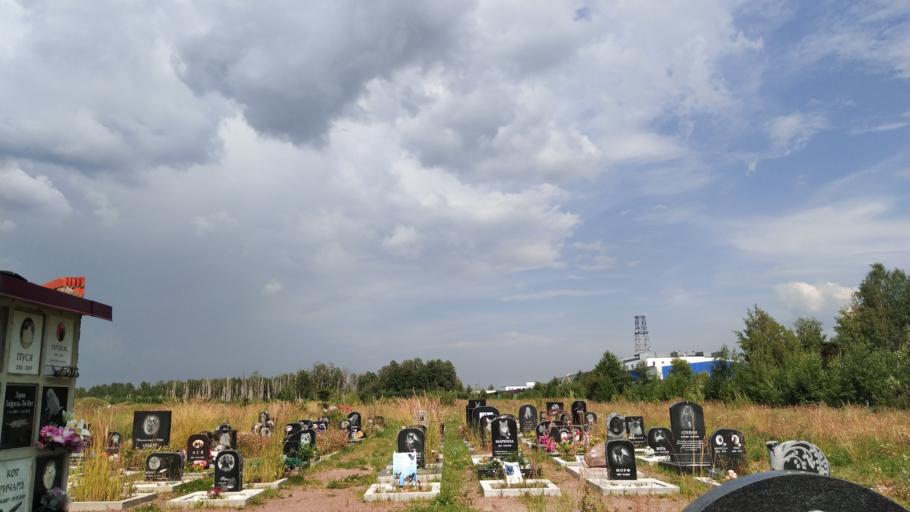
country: RU
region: St.-Petersburg
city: Krasnogvargeisky
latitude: 59.9725
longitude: 30.4714
